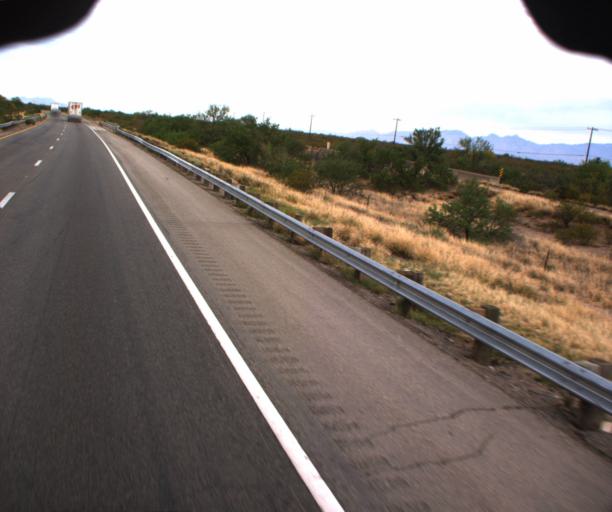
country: US
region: Arizona
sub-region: Pima County
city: Vail
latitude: 32.0417
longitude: -110.7390
